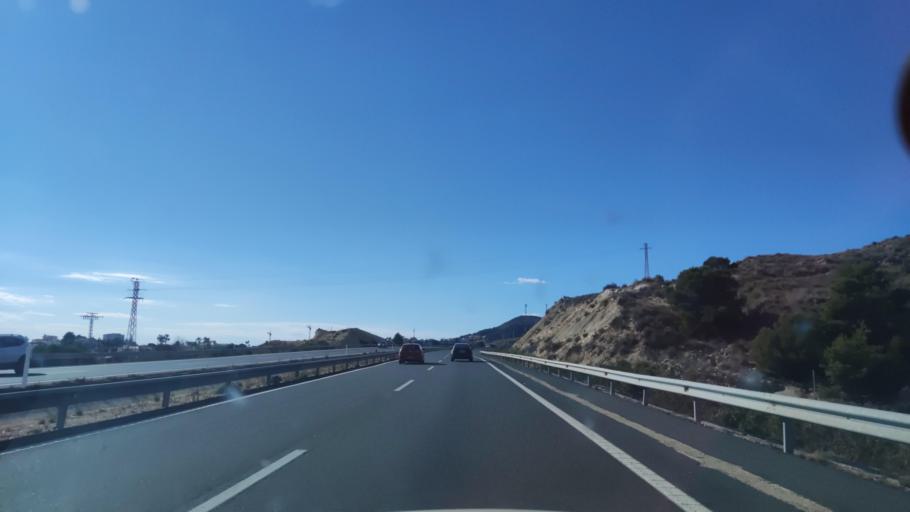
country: ES
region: Valencia
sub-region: Provincia de Alicante
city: Aiguees
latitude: 38.4821
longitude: -0.3149
